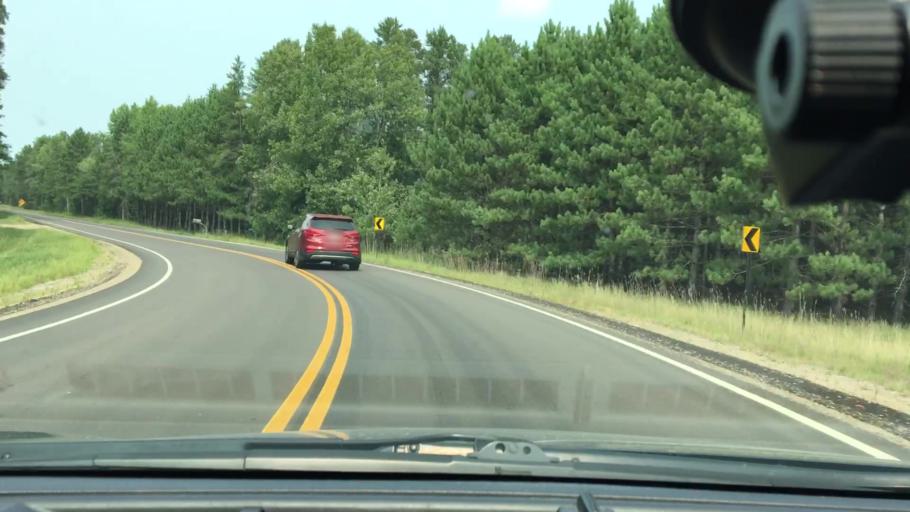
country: US
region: Minnesota
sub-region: Crow Wing County
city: Breezy Point
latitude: 46.5292
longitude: -94.1823
